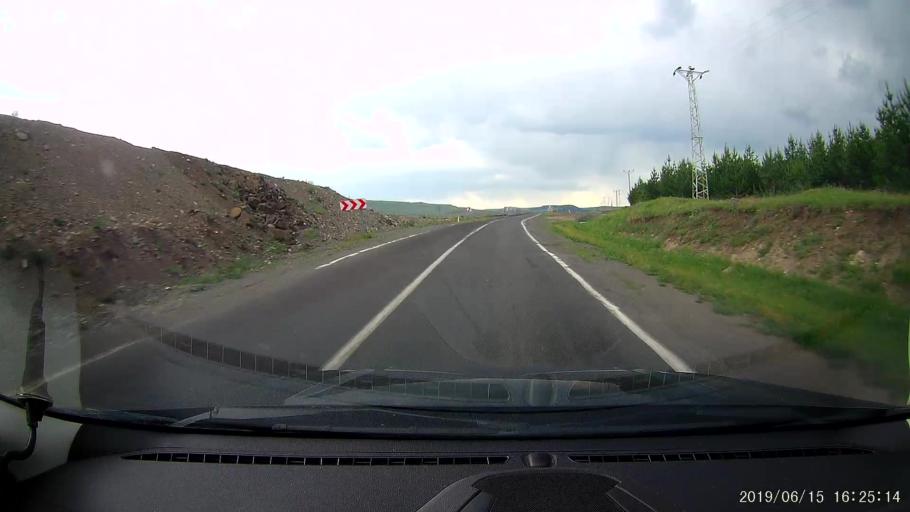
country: TR
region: Ardahan
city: Hanak
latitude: 41.1564
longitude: 42.8712
